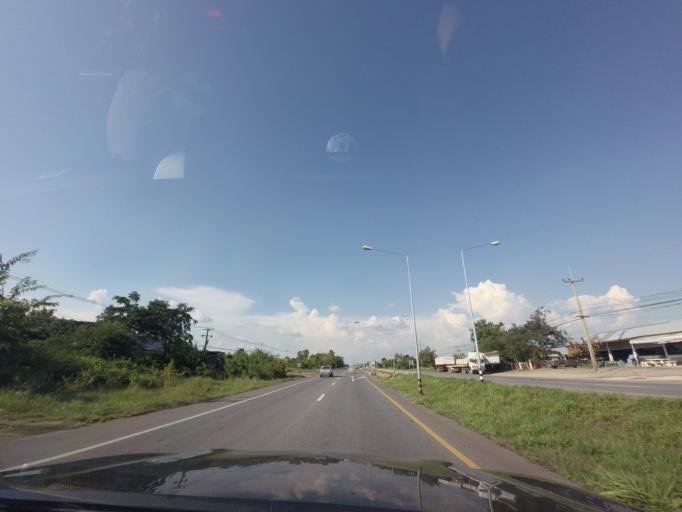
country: TH
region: Khon Kaen
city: Non Sila
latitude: 15.9822
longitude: 102.6962
